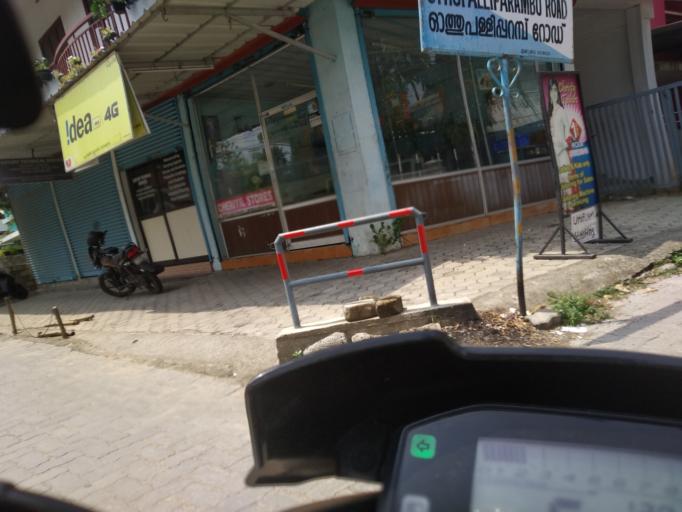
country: IN
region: Kerala
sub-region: Ernakulam
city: Elur
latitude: 10.0160
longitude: 76.3260
